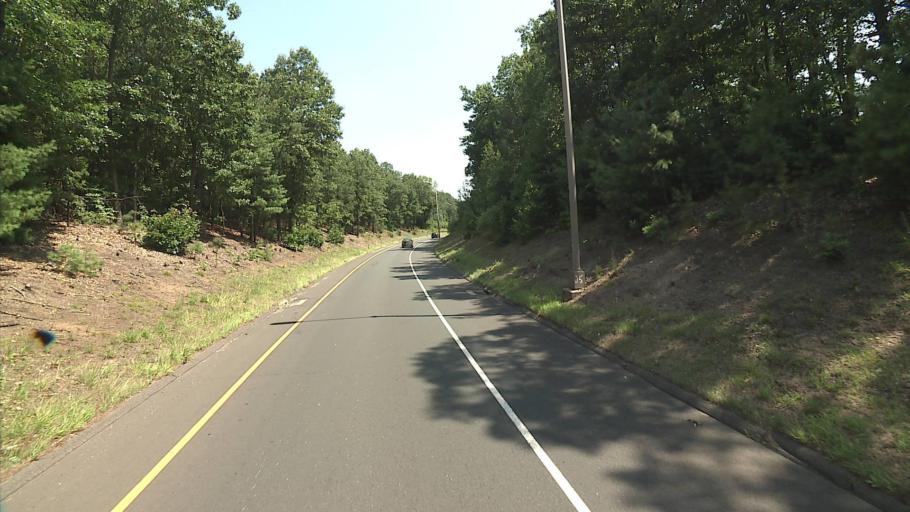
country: US
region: Connecticut
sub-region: Hartford County
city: Tariffville
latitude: 41.9241
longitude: -72.6986
